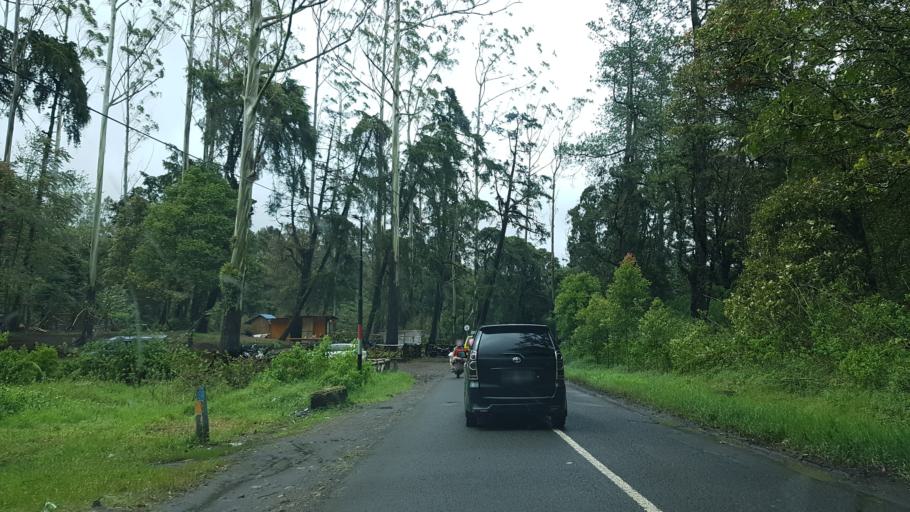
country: ID
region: West Java
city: Banjar
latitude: -7.1448
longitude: 107.3917
